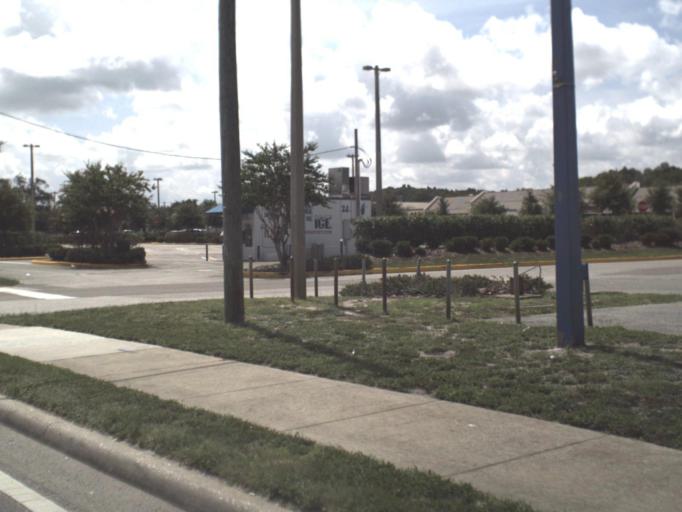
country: US
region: Florida
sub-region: Pasco County
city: Bayonet Point
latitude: 28.3310
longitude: -82.6702
